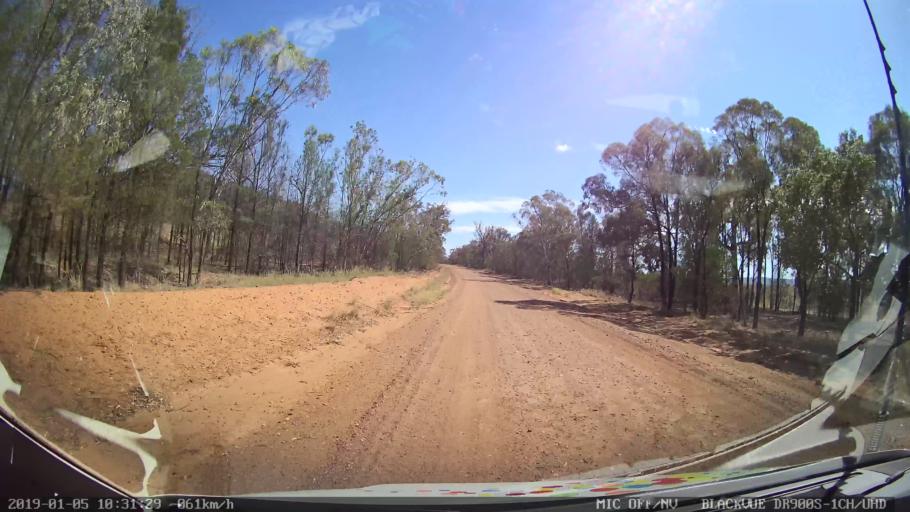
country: AU
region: New South Wales
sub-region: Gilgandra
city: Gilgandra
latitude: -31.5239
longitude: 148.9279
